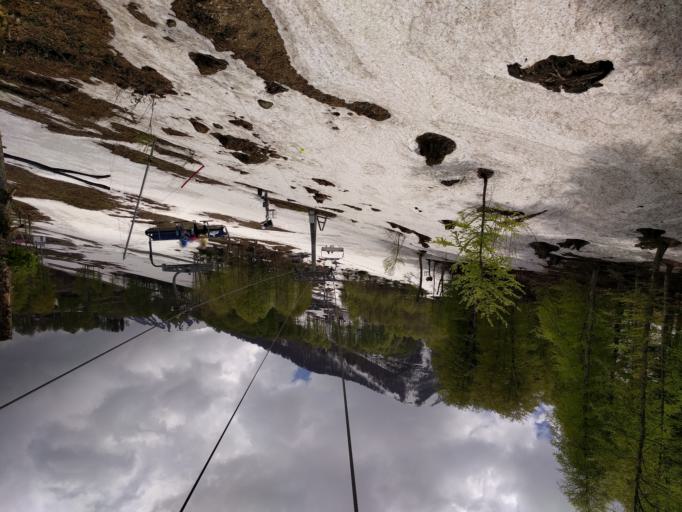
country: RU
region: Krasnodarskiy
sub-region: Sochi City
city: Krasnaya Polyana
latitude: 43.6452
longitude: 40.3237
